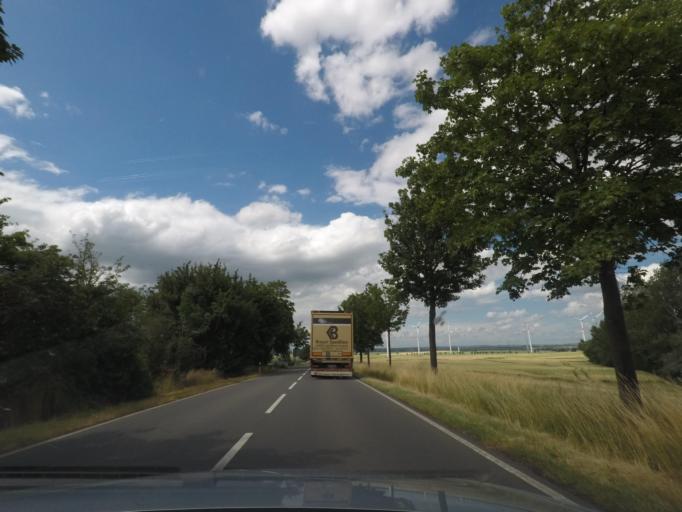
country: DE
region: Saxony-Anhalt
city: Schwanebeck
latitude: 51.9838
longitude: 11.1231
